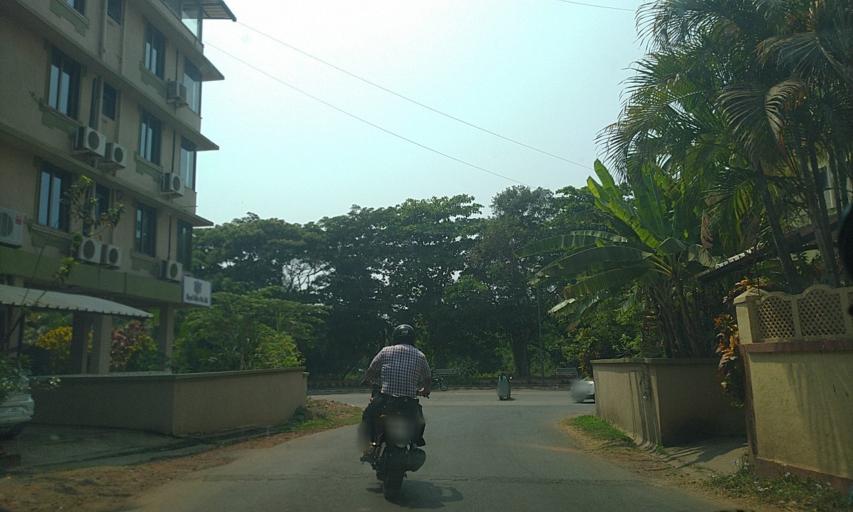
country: IN
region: Goa
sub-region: North Goa
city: Taleigao
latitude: 15.4725
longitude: 73.8087
